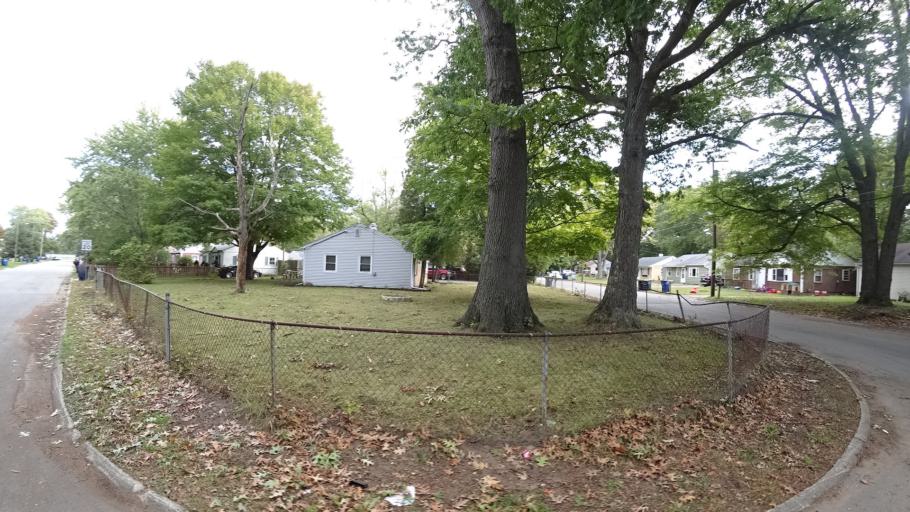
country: US
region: Indiana
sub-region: LaPorte County
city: Trail Creek
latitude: 41.7032
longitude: -86.8677
